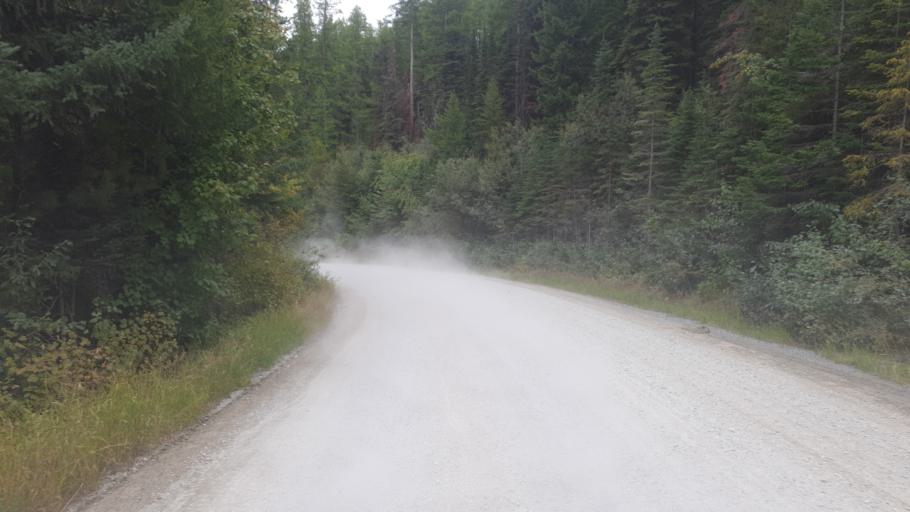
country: US
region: Montana
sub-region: Flathead County
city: Lakeside
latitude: 47.9922
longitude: -114.3254
